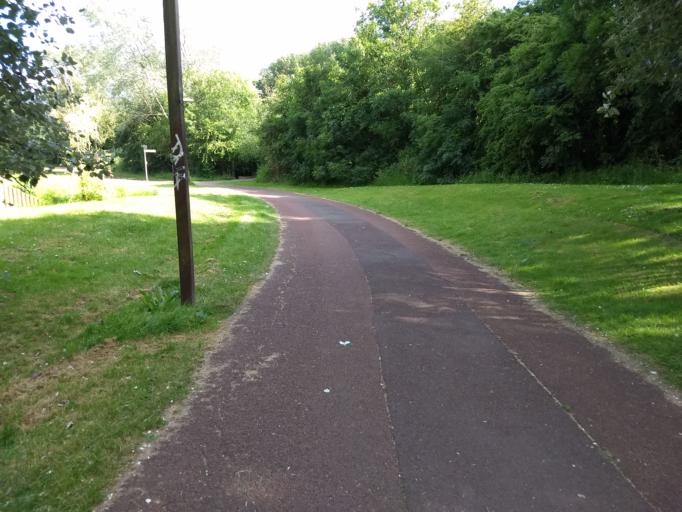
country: GB
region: England
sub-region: Milton Keynes
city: Shenley Church End
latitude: 52.0343
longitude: -0.8030
